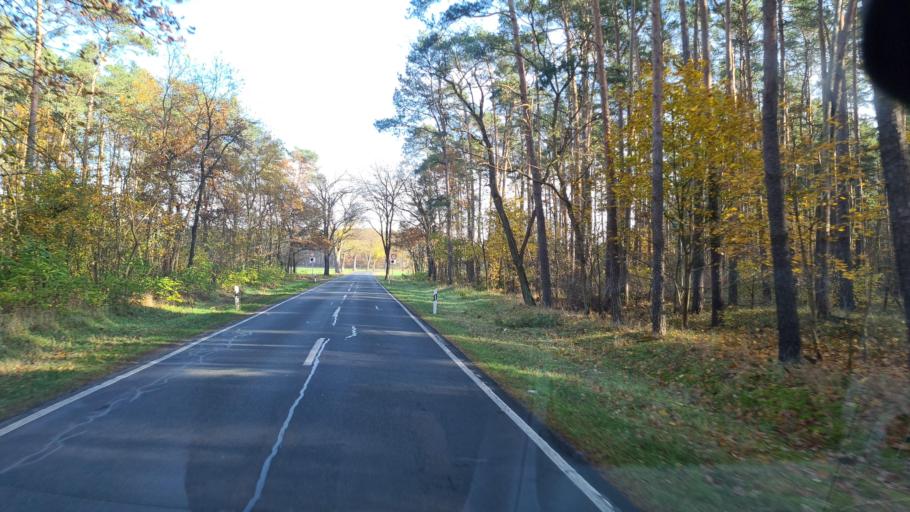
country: DE
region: Brandenburg
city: Golzow
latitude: 52.2823
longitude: 12.6228
